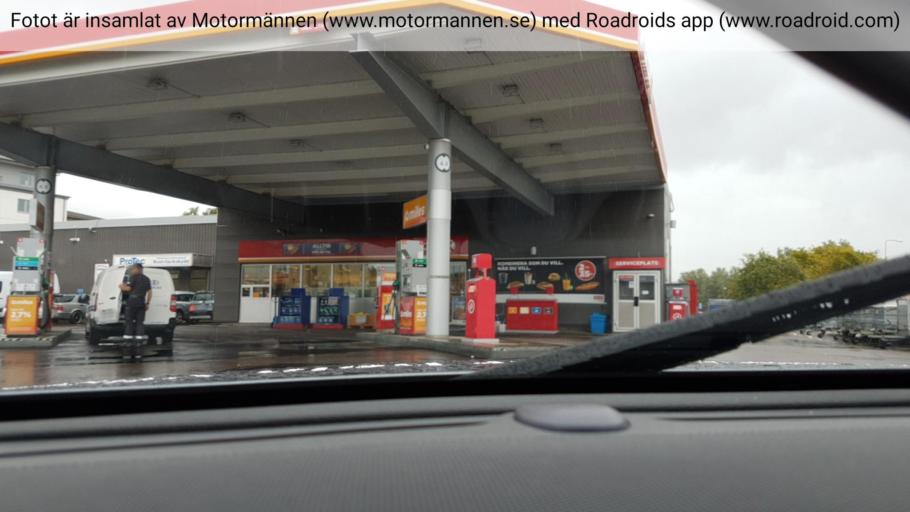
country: SE
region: Vaestra Goetaland
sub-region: Molndal
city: Moelndal
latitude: 57.6486
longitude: 12.0170
